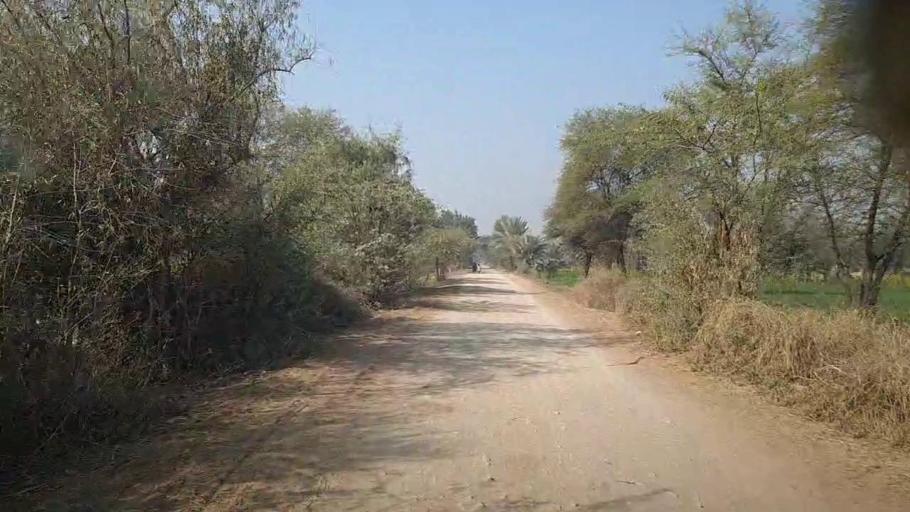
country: PK
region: Sindh
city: Karaundi
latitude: 26.8459
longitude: 68.3839
